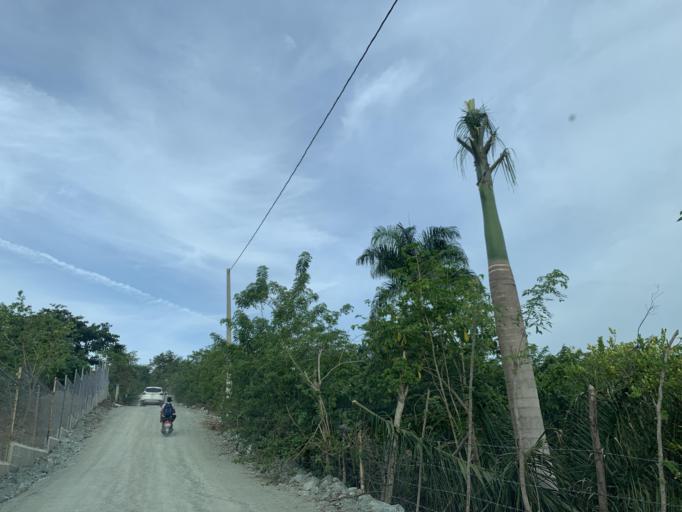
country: DO
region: Santiago
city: Pedro Garcia
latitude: 19.6979
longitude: -70.6185
